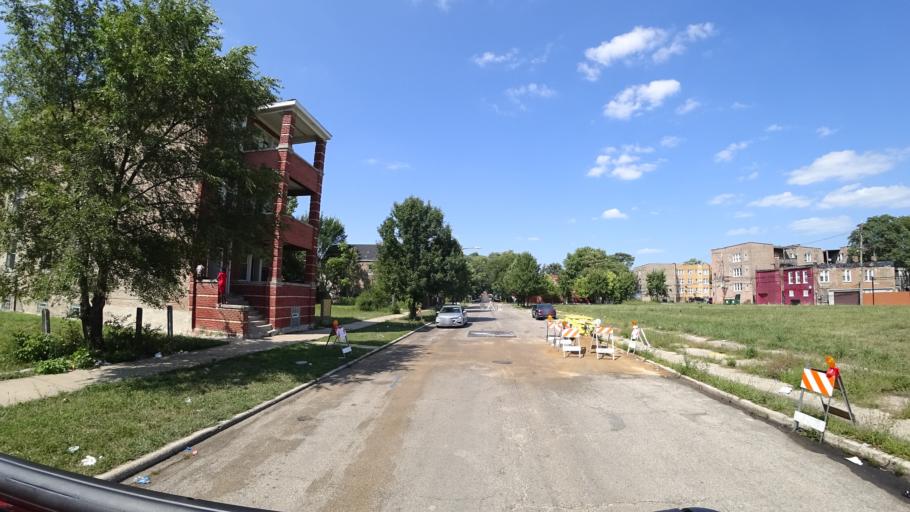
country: US
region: Illinois
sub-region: Cook County
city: Cicero
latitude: 41.8635
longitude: -87.7287
